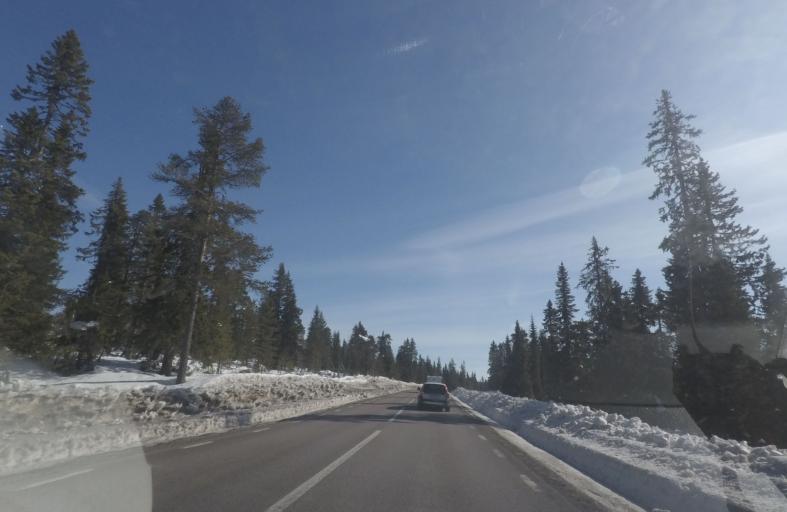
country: NO
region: Hedmark
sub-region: Trysil
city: Innbygda
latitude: 61.1757
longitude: 13.0651
